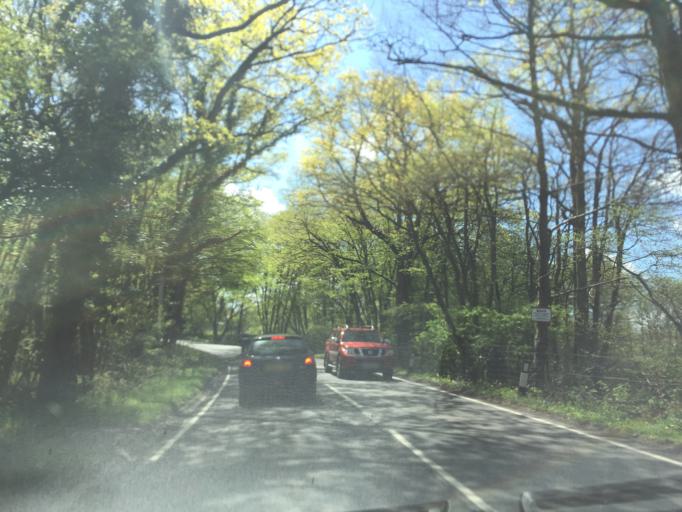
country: GB
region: England
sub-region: Kent
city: Edenbridge
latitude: 51.1339
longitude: 0.1069
